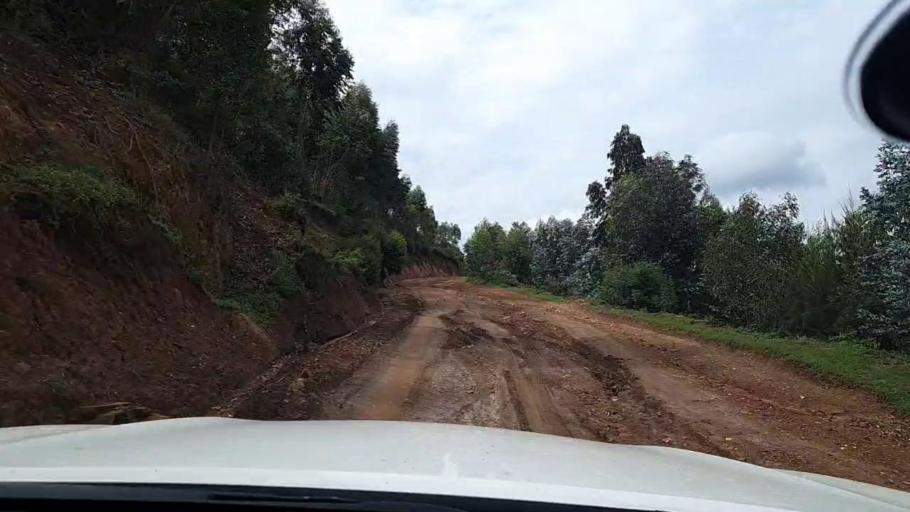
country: RW
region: Western Province
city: Kibuye
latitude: -2.1284
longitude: 29.3745
